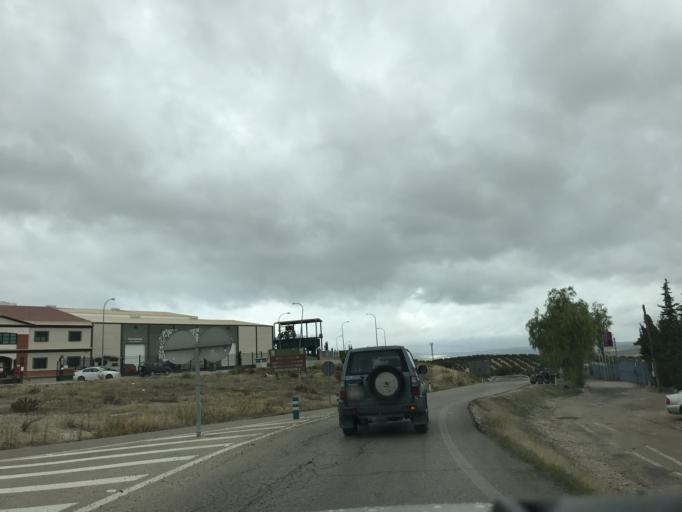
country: ES
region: Andalusia
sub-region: Provincia de Jaen
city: Peal de Becerro
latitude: 37.9189
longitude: -3.1318
